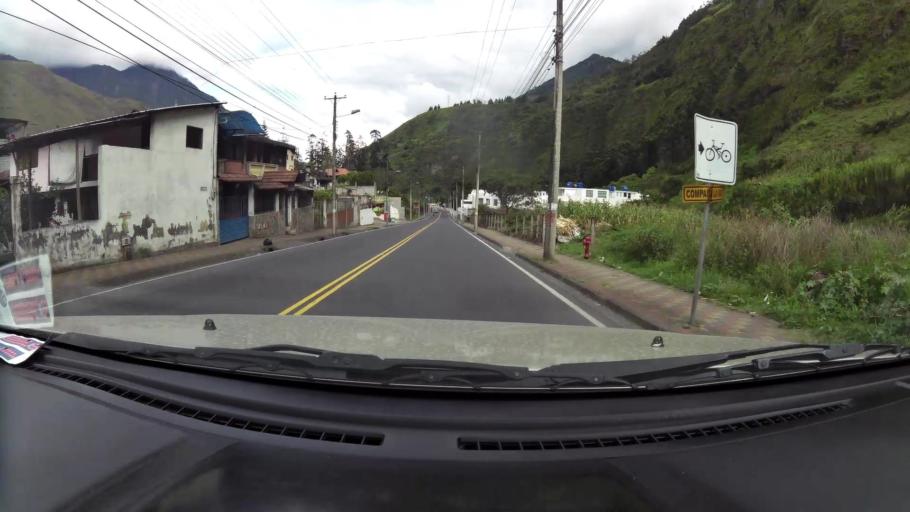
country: EC
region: Tungurahua
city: Banos
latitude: -1.3946
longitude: -78.4107
